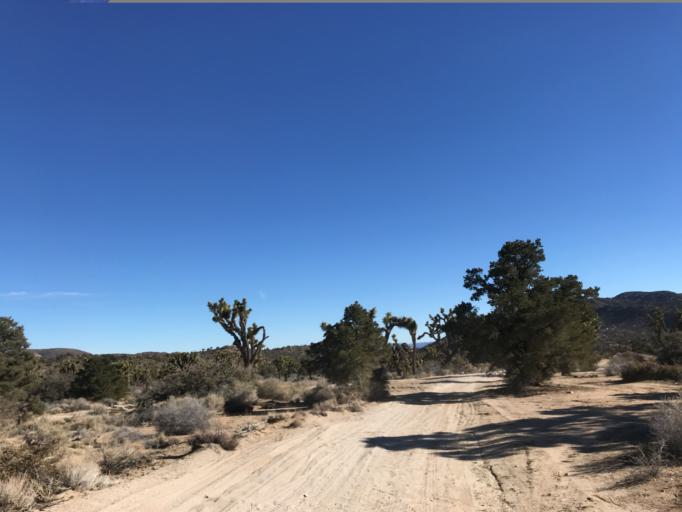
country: US
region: California
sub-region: San Bernardino County
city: Morongo Valley
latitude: 34.2339
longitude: -116.6449
